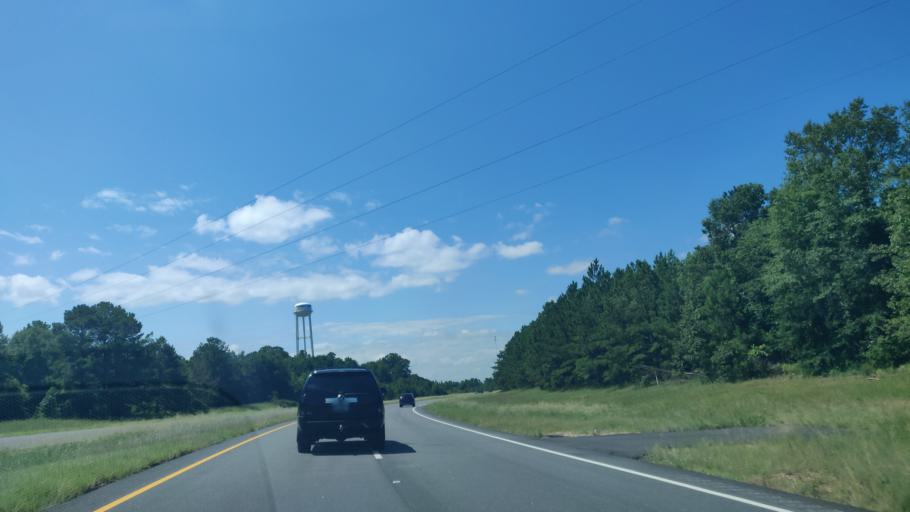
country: US
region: Georgia
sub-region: Stewart County
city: Richland
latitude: 32.1458
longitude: -84.6873
